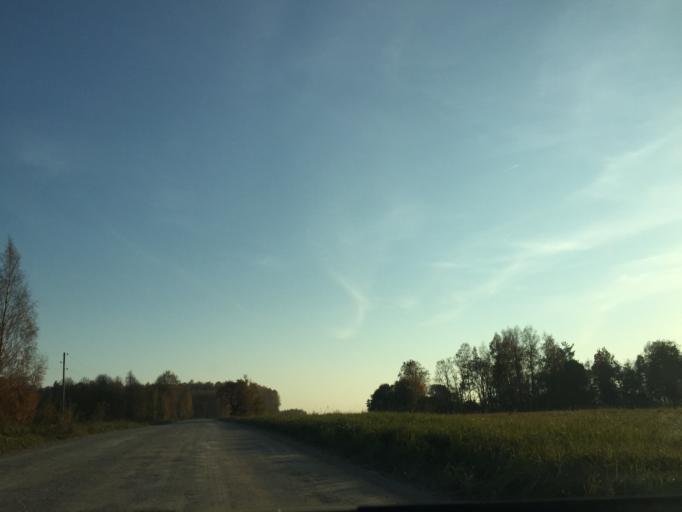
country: LV
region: Vainode
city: Vainode
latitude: 56.5415
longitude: 21.8368
